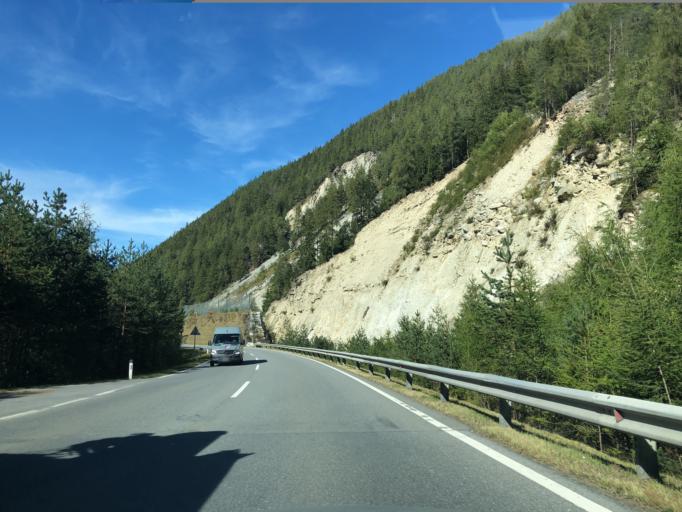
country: AT
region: Tyrol
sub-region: Politischer Bezirk Imst
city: Umhausen
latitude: 47.1161
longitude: 10.9361
